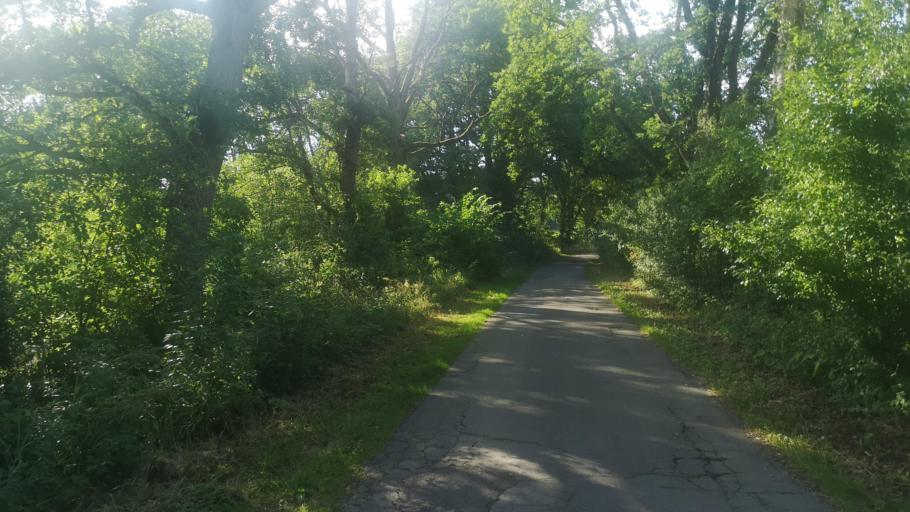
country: DE
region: Lower Saxony
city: Dahlenburg
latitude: 53.2063
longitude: 10.7159
